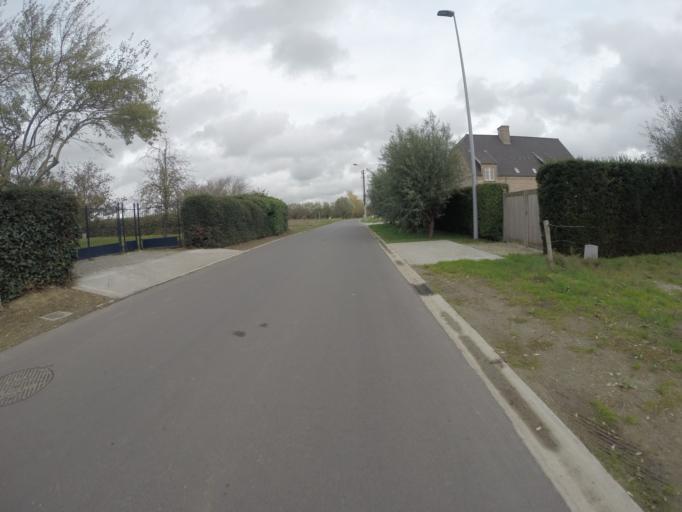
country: BE
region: Flanders
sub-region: Provincie Oost-Vlaanderen
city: Knesselare
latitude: 51.1453
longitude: 3.3899
